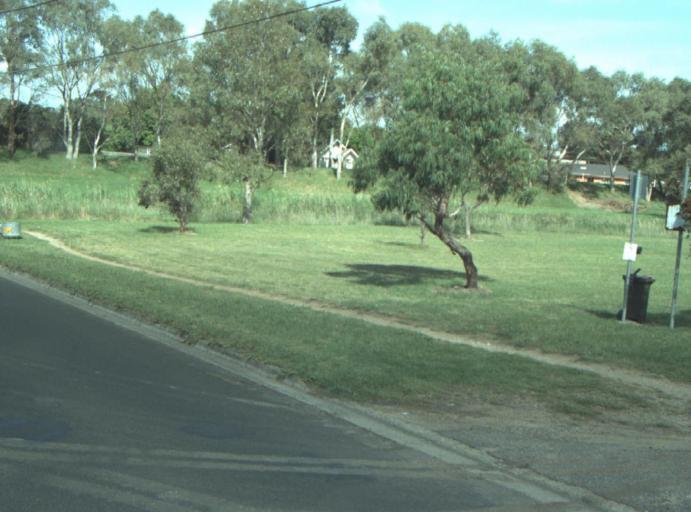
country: AU
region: Victoria
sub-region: Greater Geelong
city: Lara
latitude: -38.0191
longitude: 144.4031
